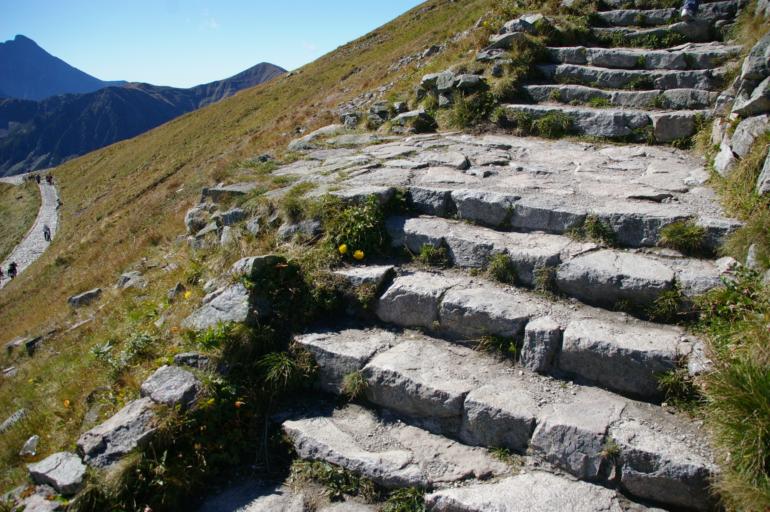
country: PL
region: Lesser Poland Voivodeship
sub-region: Powiat tatrzanski
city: Zakopane
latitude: 49.2324
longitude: 19.9815
